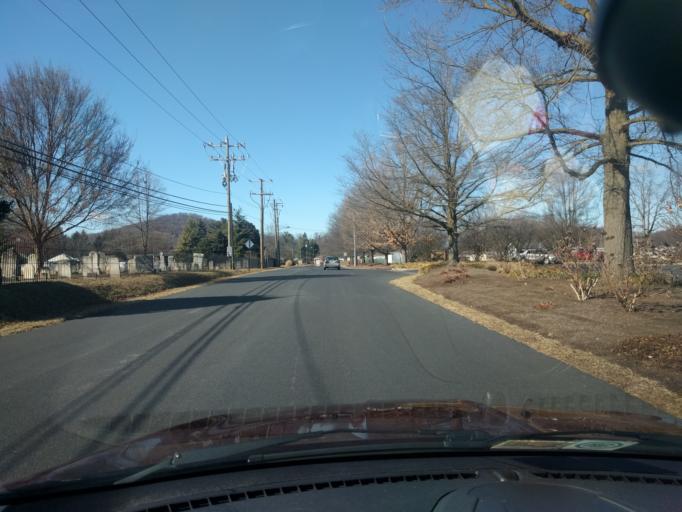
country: US
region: Virginia
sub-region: Rockingham County
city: Bridgewater
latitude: 38.3850
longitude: -78.9748
